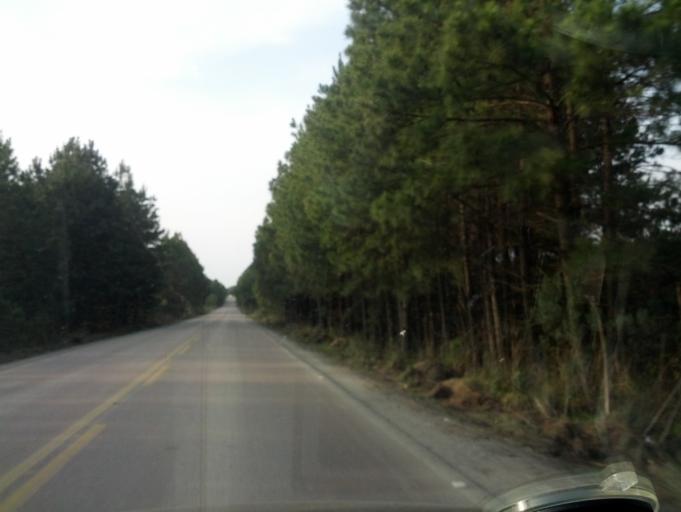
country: BR
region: Santa Catarina
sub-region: Otacilio Costa
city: Otacilio Costa
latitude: -27.4405
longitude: -50.1252
